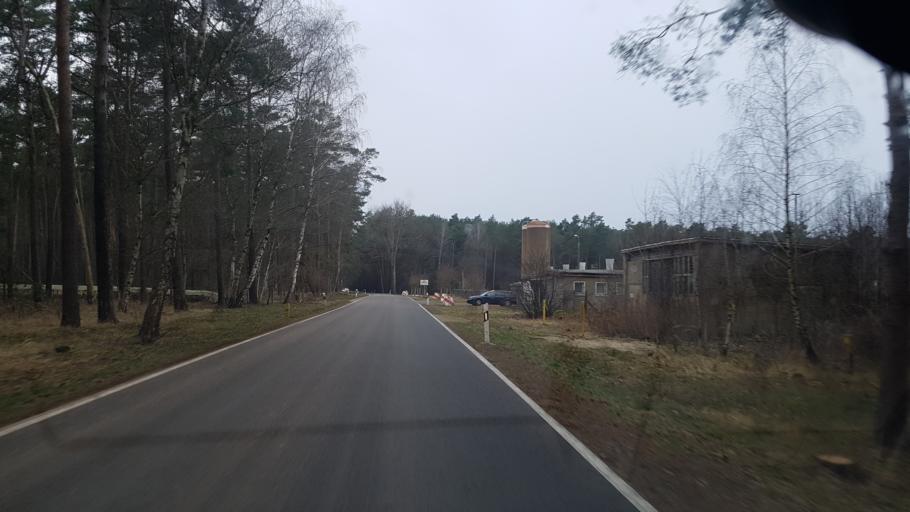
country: DE
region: Brandenburg
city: Cottbus
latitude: 51.6997
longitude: 14.4443
